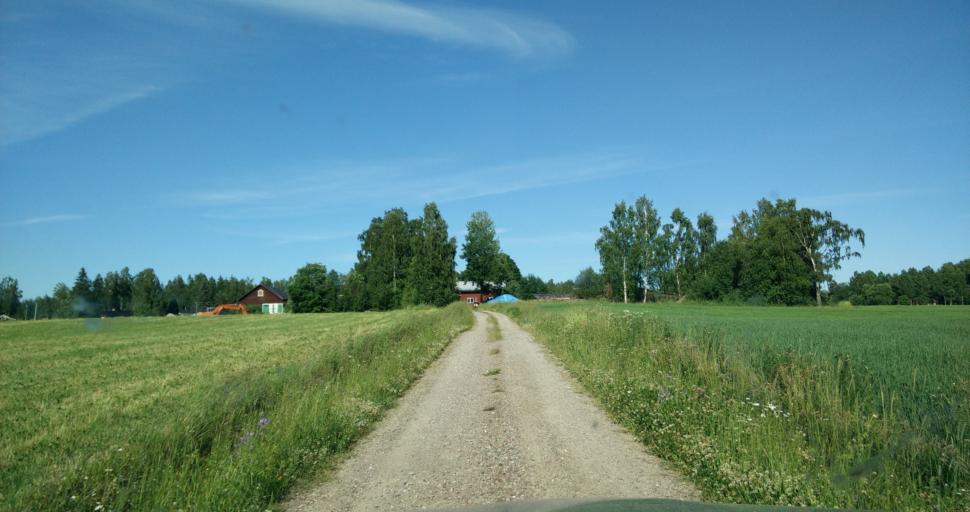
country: SE
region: Dalarna
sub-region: Hedemora Kommun
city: Langshyttan
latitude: 60.3901
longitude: 15.9582
